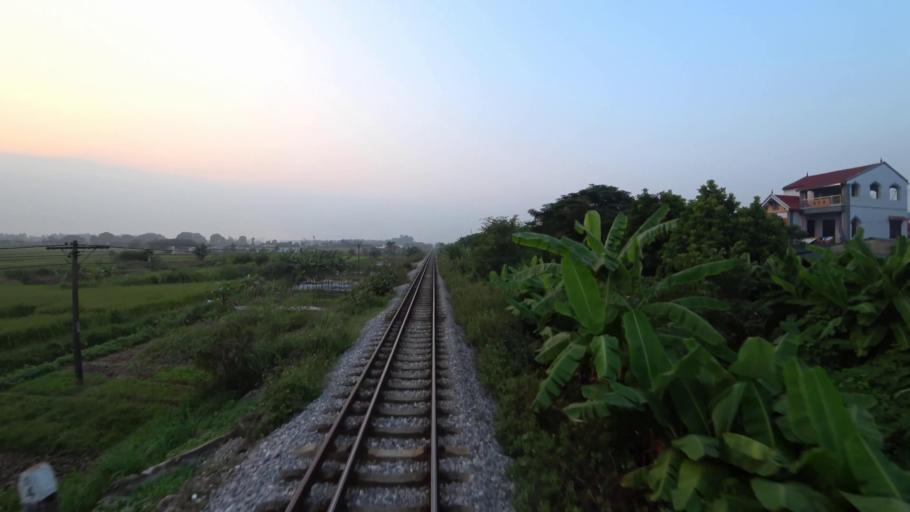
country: VN
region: Ha Noi
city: Dong Anh
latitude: 21.1290
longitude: 105.8775
